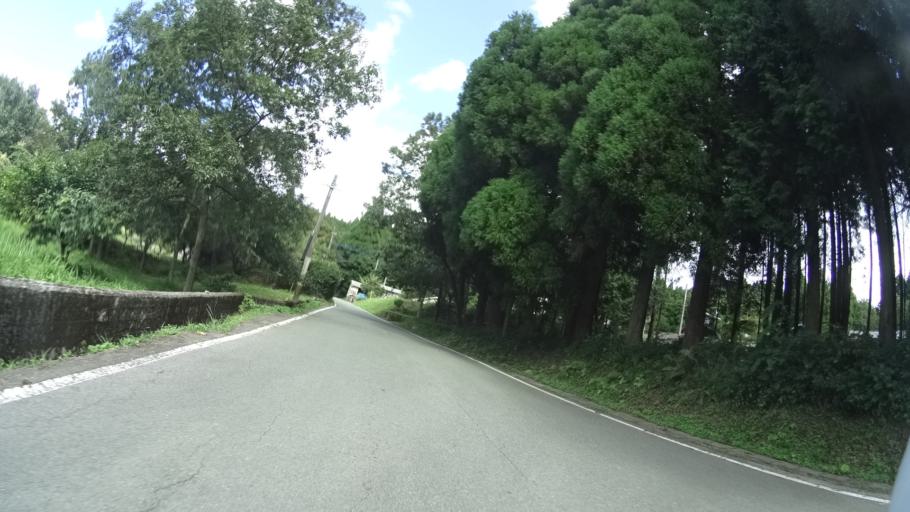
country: JP
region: Kumamoto
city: Aso
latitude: 32.8124
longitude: 131.1312
